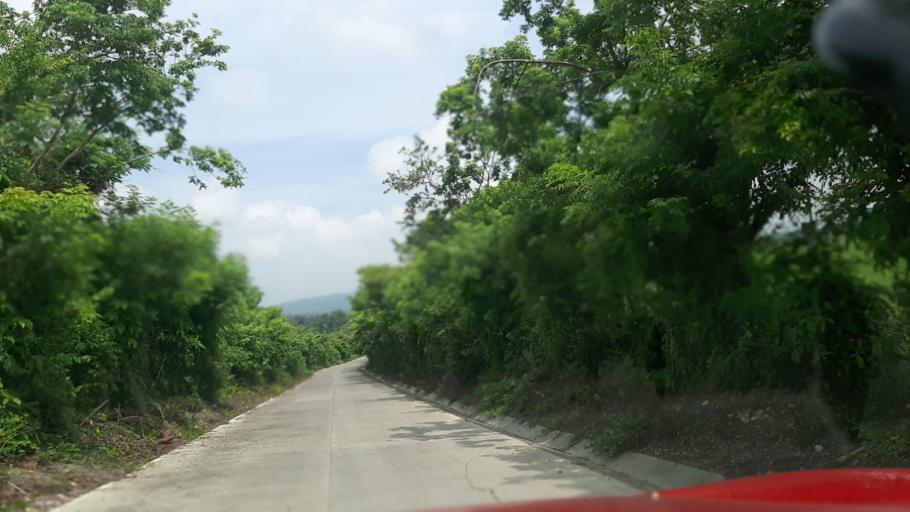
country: MX
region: Veracruz
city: Gutierrez Zamora
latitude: 20.4460
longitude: -97.1740
